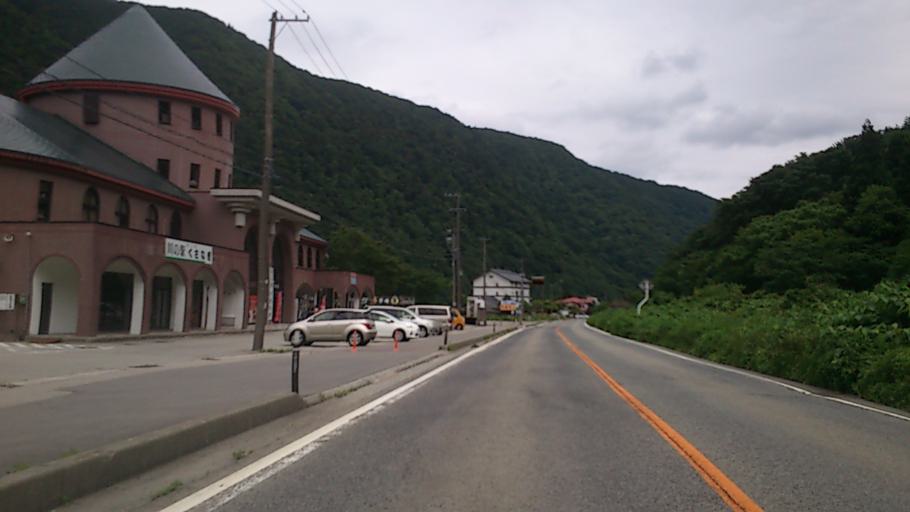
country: JP
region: Yamagata
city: Tsuruoka
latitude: 38.7668
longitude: 140.0491
